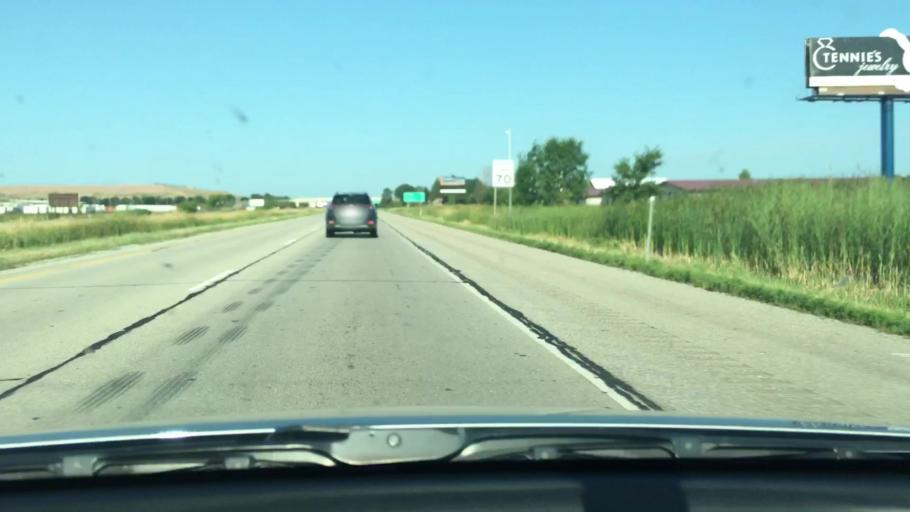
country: US
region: Wisconsin
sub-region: Outagamie County
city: Little Chute
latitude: 44.2980
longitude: -88.3252
